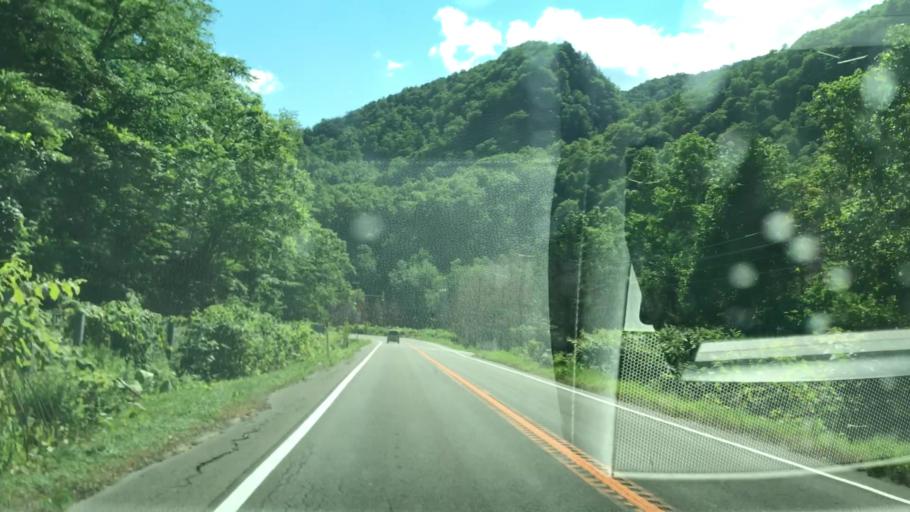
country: JP
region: Hokkaido
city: Shimo-furano
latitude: 42.9191
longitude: 142.5878
